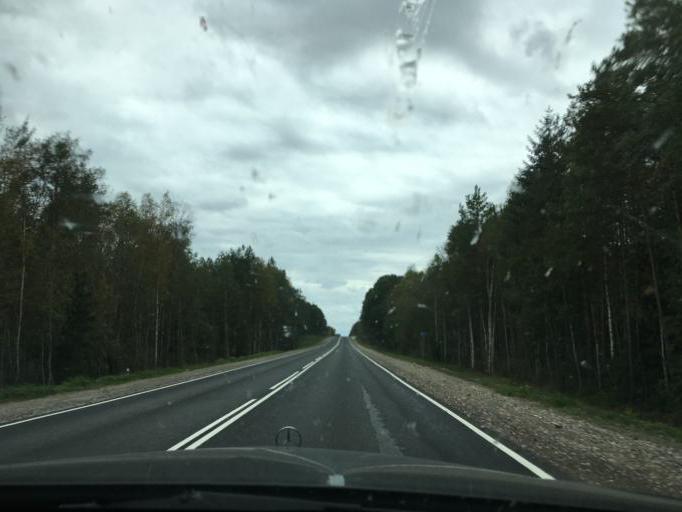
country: RU
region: Pskov
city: Pechory
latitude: 57.6717
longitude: 27.5344
